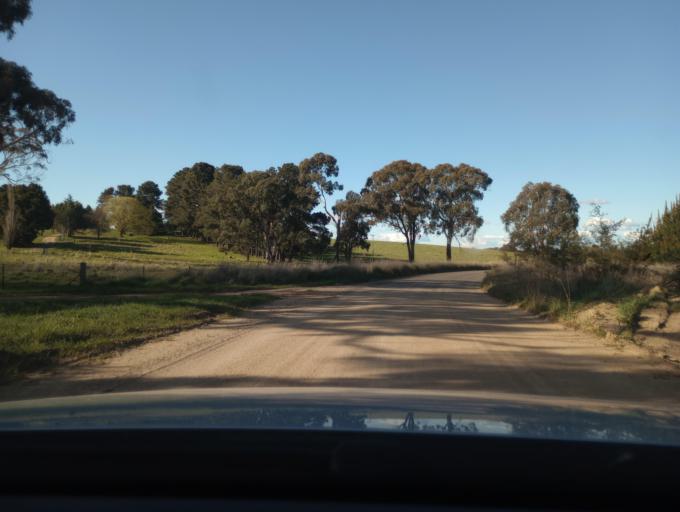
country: AU
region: New South Wales
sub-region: Blayney
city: Millthorpe
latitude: -33.4132
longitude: 149.3020
